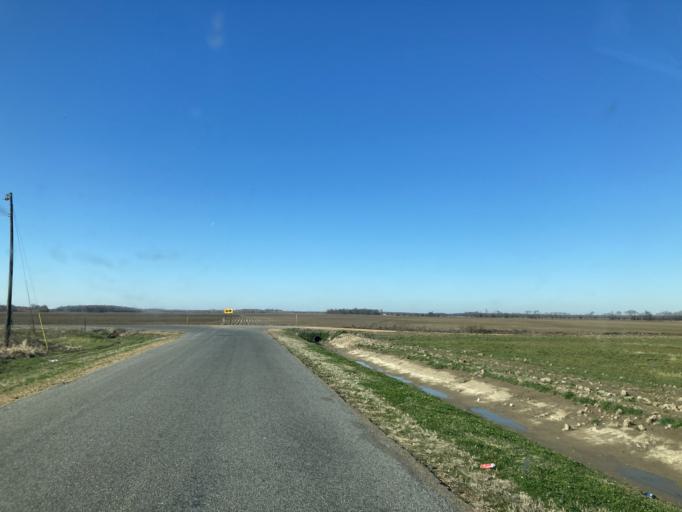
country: US
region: Mississippi
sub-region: Yazoo County
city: Yazoo City
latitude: 32.9775
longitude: -90.6043
